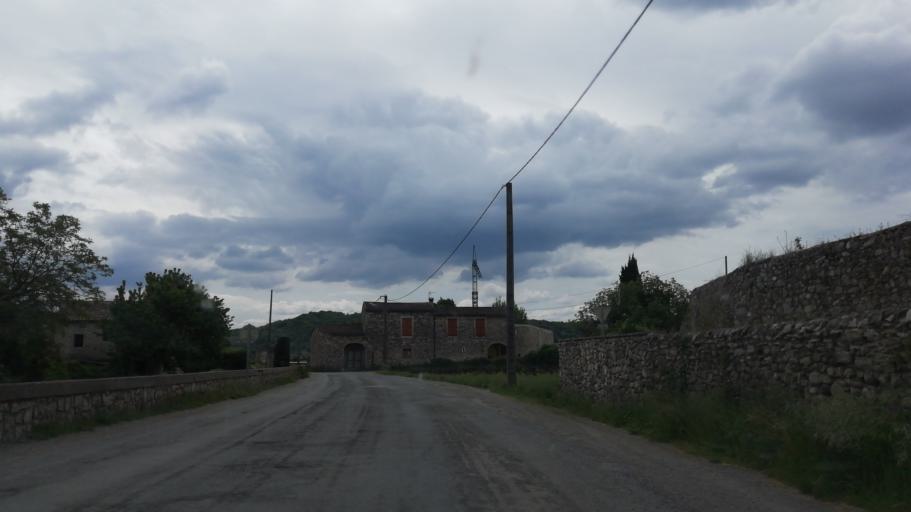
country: FR
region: Languedoc-Roussillon
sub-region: Departement de l'Herault
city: Ganges
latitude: 43.9275
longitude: 3.7041
